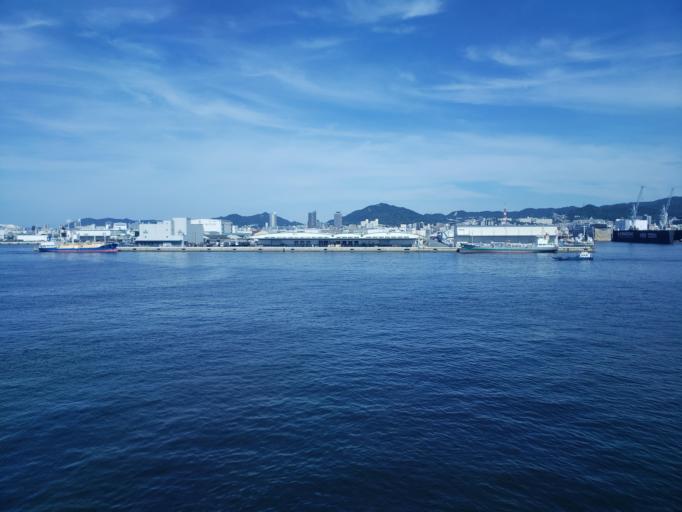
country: JP
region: Hyogo
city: Kobe
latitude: 34.6649
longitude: 135.1911
